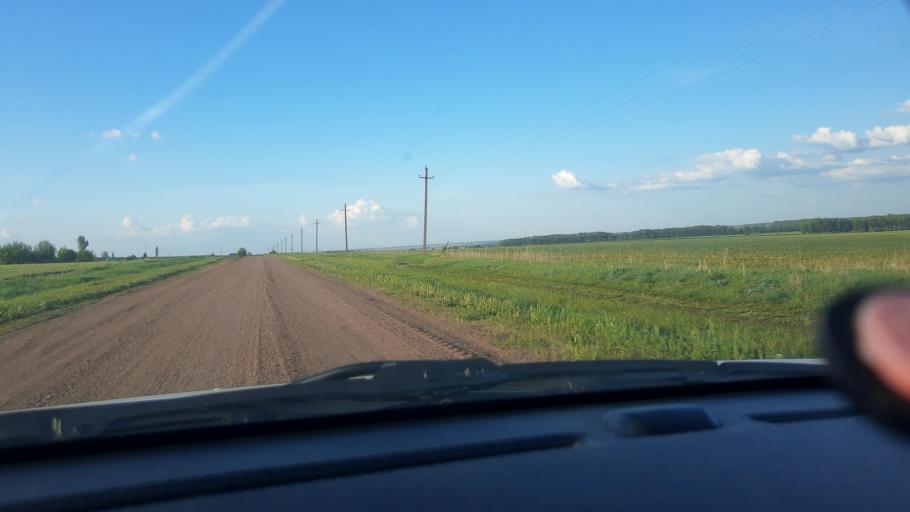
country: RU
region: Bashkortostan
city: Karmaskaly
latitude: 54.3865
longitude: 55.9422
